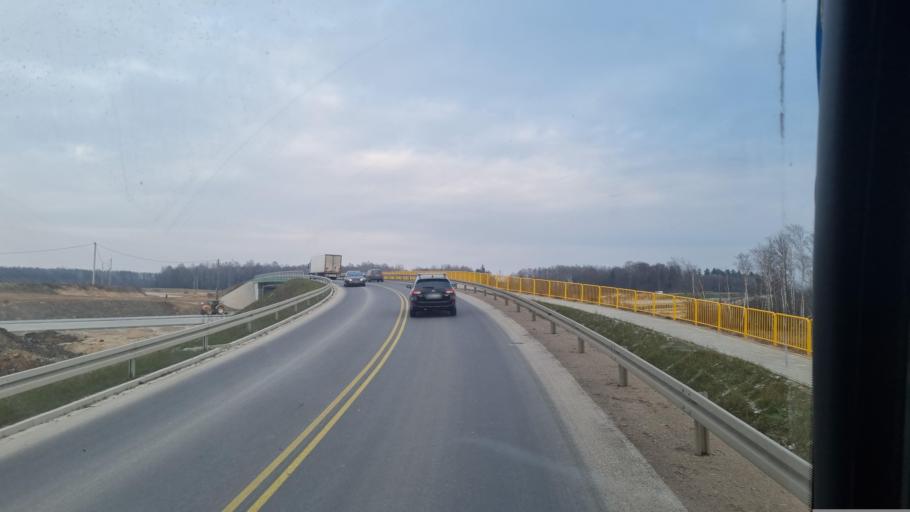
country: PL
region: Warmian-Masurian Voivodeship
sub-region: Powiat elcki
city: Elk
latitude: 53.8543
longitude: 22.4955
